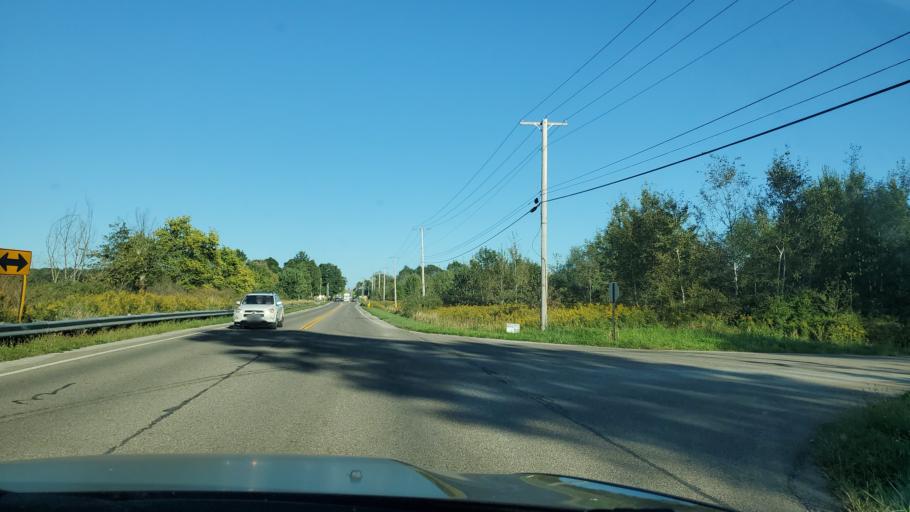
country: US
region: Ohio
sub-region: Mahoning County
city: Canfield
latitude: 40.9882
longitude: -80.7640
